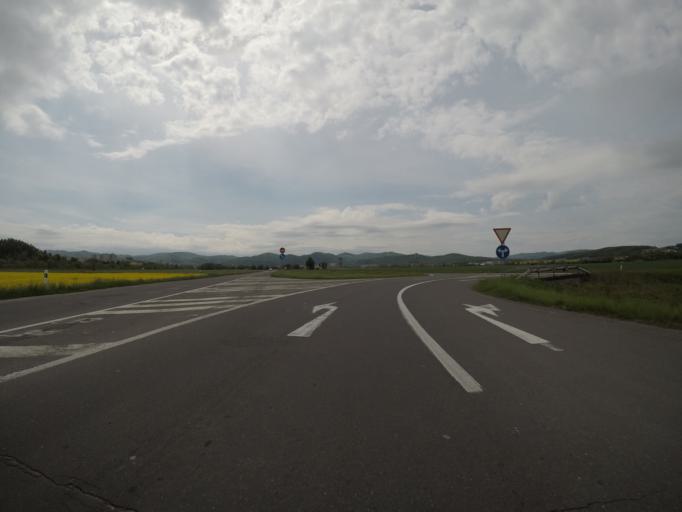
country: SK
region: Banskobystricky
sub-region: Okres Banska Bystrica
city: Zvolen
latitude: 48.6024
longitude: 19.1252
